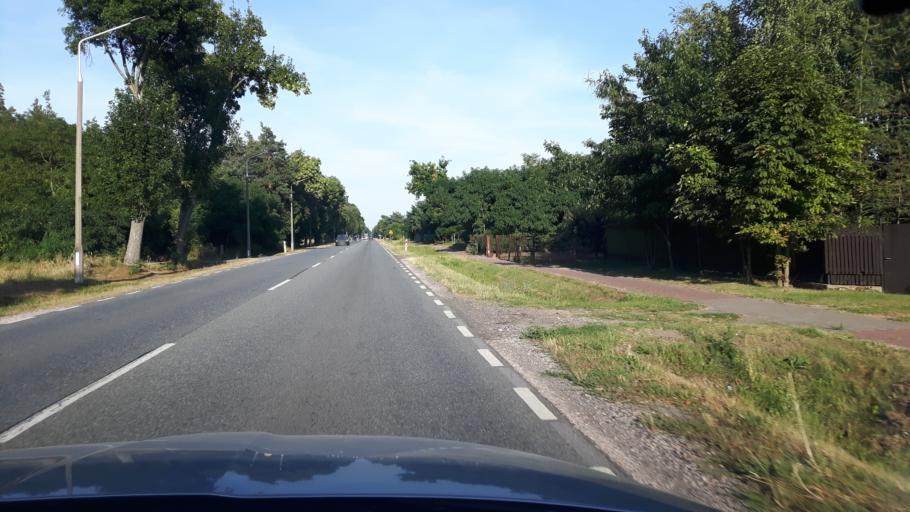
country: PL
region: Masovian Voivodeship
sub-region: Powiat legionowski
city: Wieliszew
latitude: 52.5004
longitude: 20.9271
